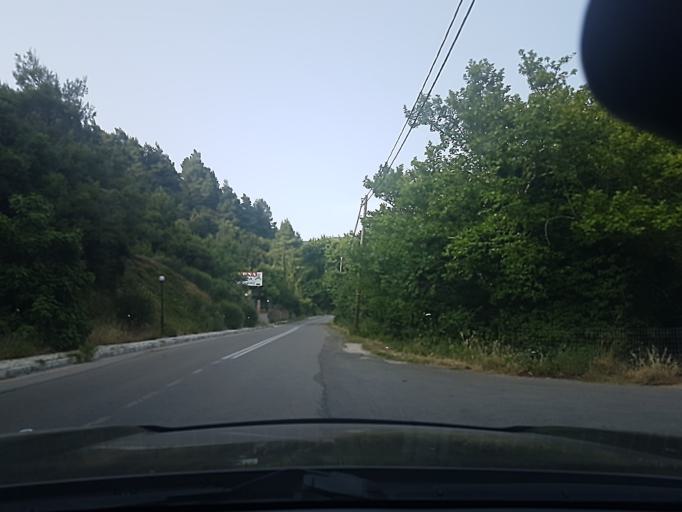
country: GR
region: Central Greece
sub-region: Nomos Evvoias
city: Yimnon
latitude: 38.5839
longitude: 23.8410
